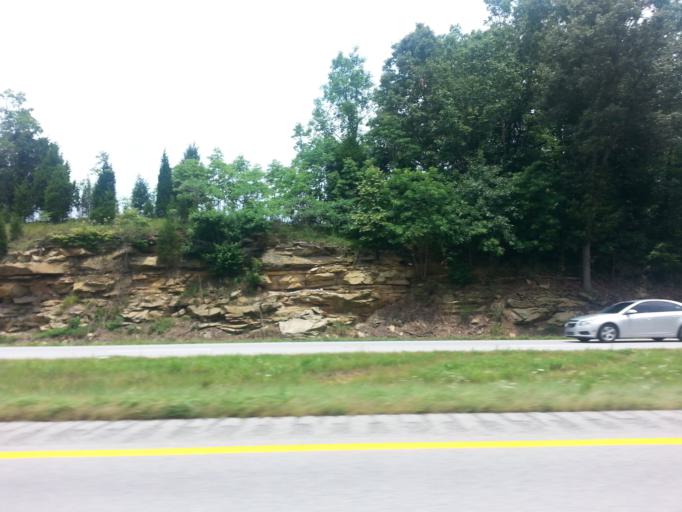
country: US
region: Kentucky
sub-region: Grayson County
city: Leitchfield
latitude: 37.5525
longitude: -86.0923
